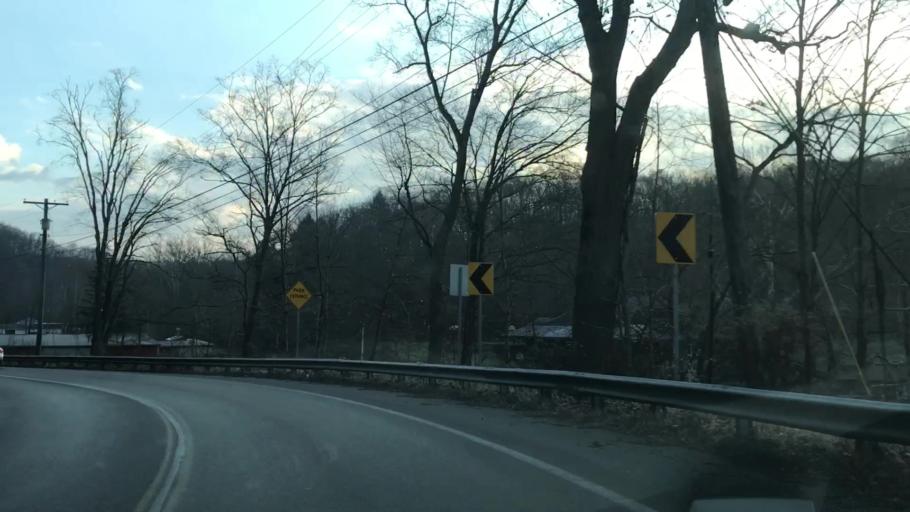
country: US
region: Pennsylvania
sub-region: Allegheny County
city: Ben Avon
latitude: 40.5216
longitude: -80.0857
